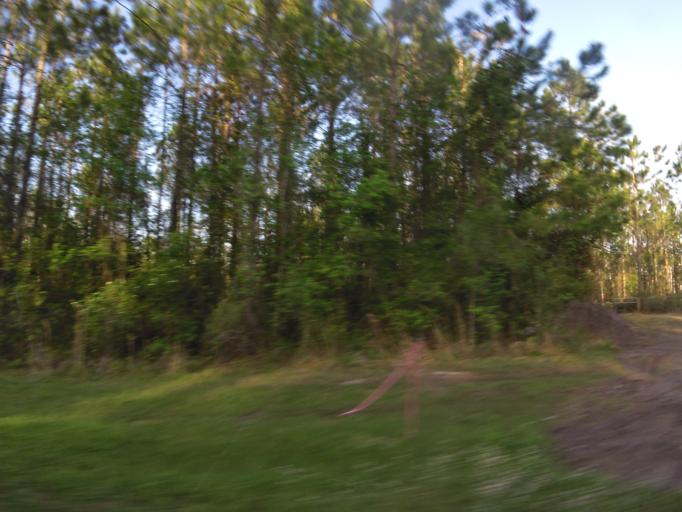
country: US
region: Florida
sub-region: Saint Johns County
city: Fruit Cove
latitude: 30.0827
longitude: -81.5295
